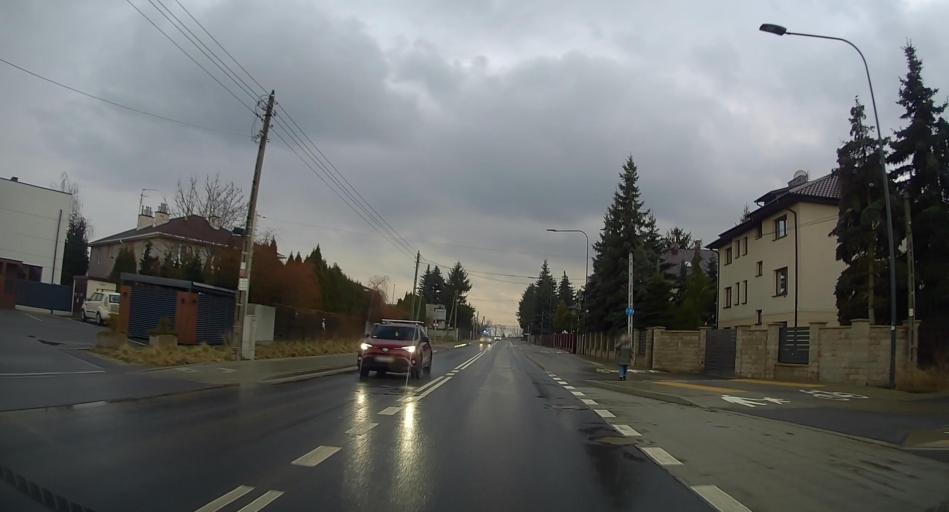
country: PL
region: Masovian Voivodeship
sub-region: Warszawa
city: Wawer
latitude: 52.1897
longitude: 21.1409
